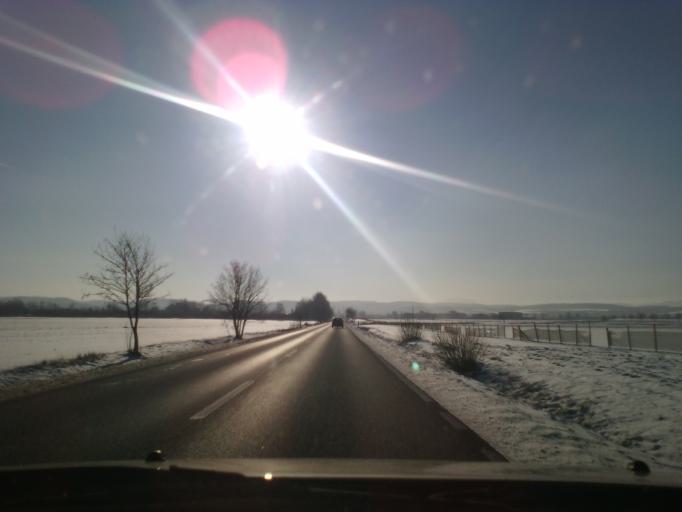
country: PL
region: Lower Silesian Voivodeship
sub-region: Powiat swidnicki
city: Swiebodzice
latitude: 50.8857
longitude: 16.3397
